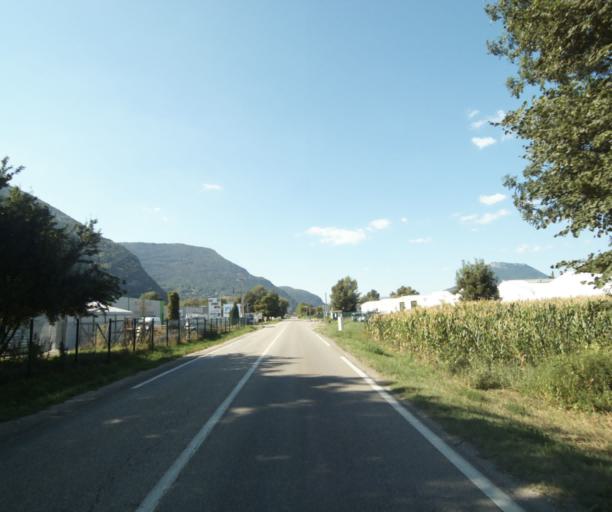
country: FR
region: Rhone-Alpes
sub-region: Departement de l'Isere
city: Noyarey
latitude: 45.2555
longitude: 5.6284
